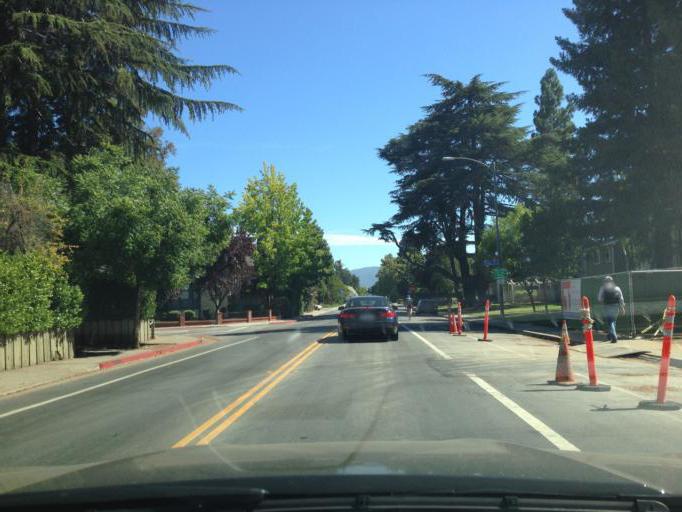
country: US
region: California
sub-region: Santa Clara County
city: Cupertino
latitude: 37.3211
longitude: -122.0232
